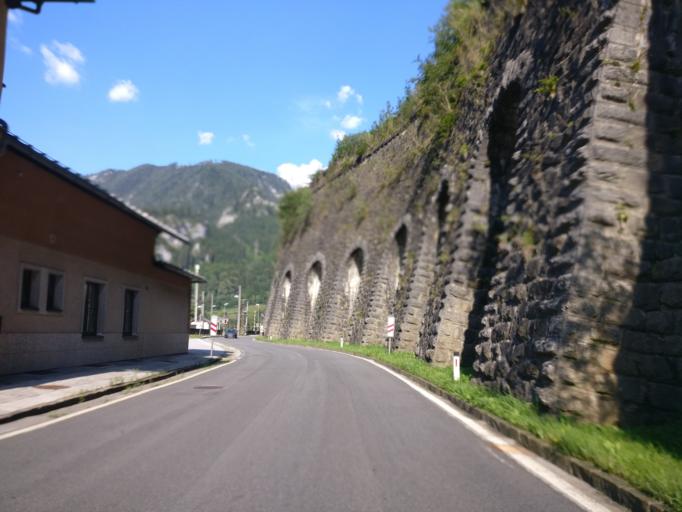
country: AT
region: Styria
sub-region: Politischer Bezirk Leoben
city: Hieflau
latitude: 47.6074
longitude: 14.7377
